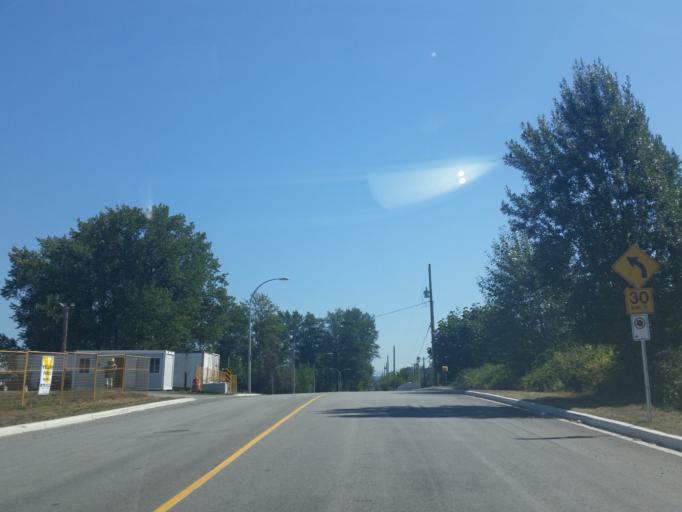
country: CA
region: British Columbia
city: Langley
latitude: 49.0971
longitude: -122.7000
